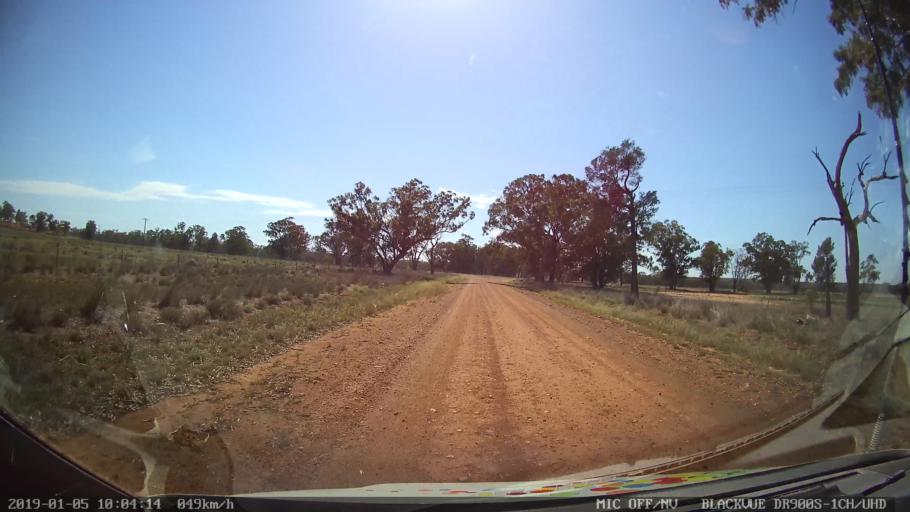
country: AU
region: New South Wales
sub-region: Gilgandra
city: Gilgandra
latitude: -31.6728
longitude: 148.8592
